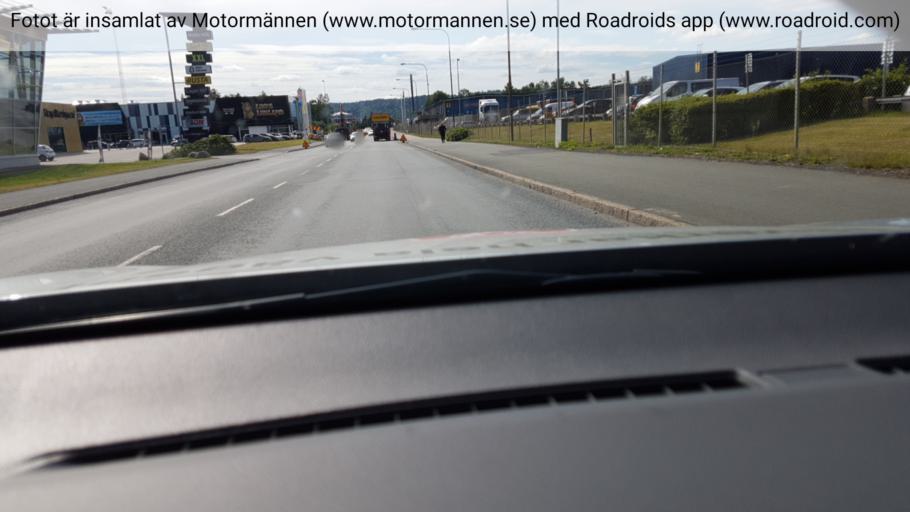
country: SE
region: Joenkoeping
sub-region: Jonkopings Kommun
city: Jonkoping
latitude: 57.7617
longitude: 14.1749
